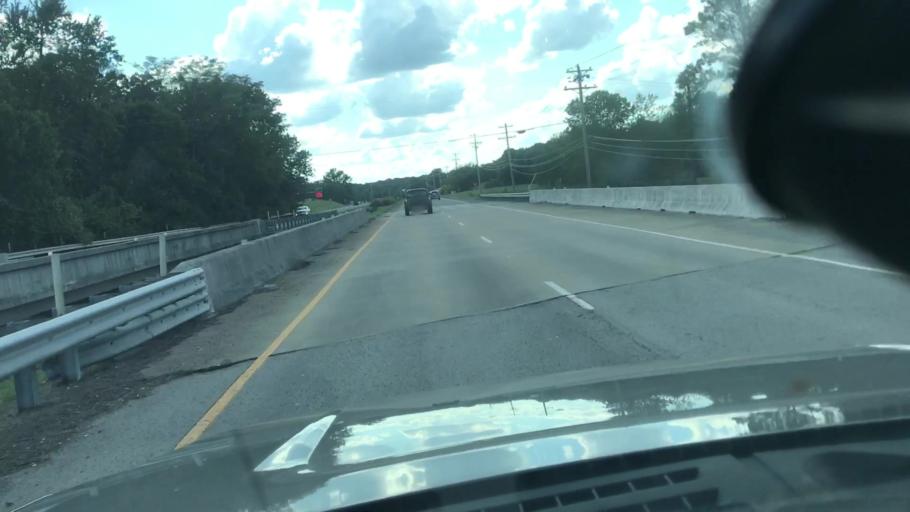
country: US
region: Tennessee
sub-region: Williamson County
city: Fairview
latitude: 35.9843
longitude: -87.1146
